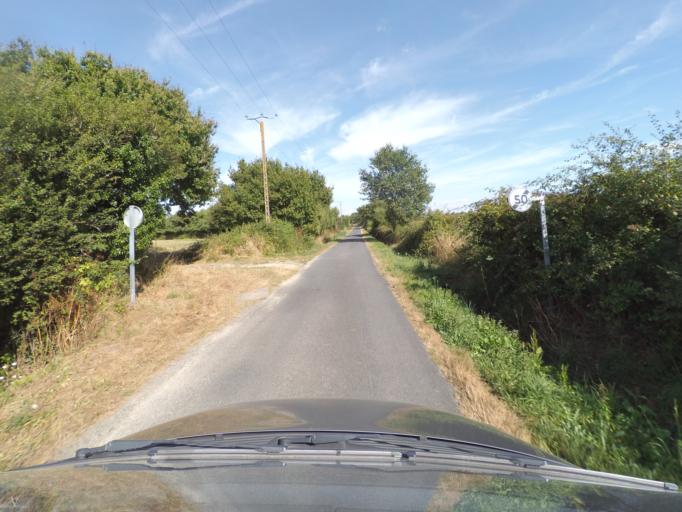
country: FR
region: Pays de la Loire
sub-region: Departement de la Loire-Atlantique
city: Le Bignon
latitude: 47.0909
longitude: -1.4702
